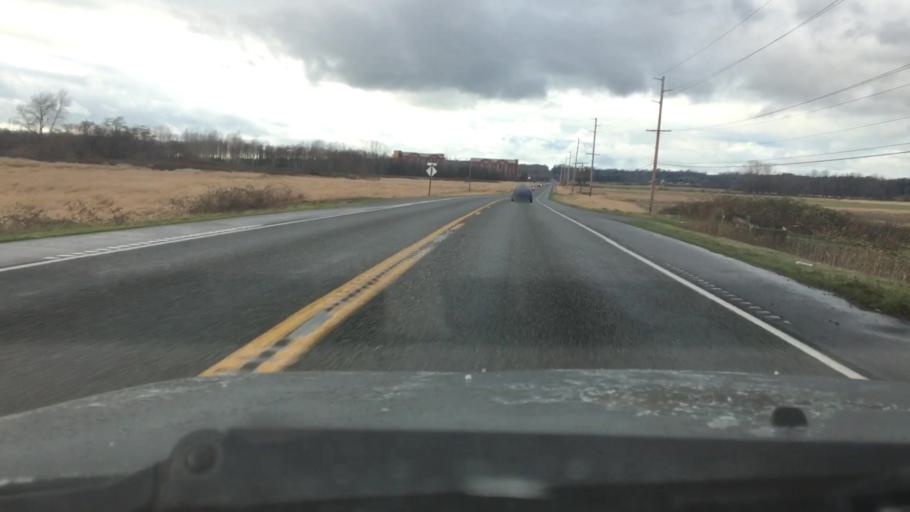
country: US
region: Washington
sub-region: Whatcom County
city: Ferndale
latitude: 48.8191
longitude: -122.6134
